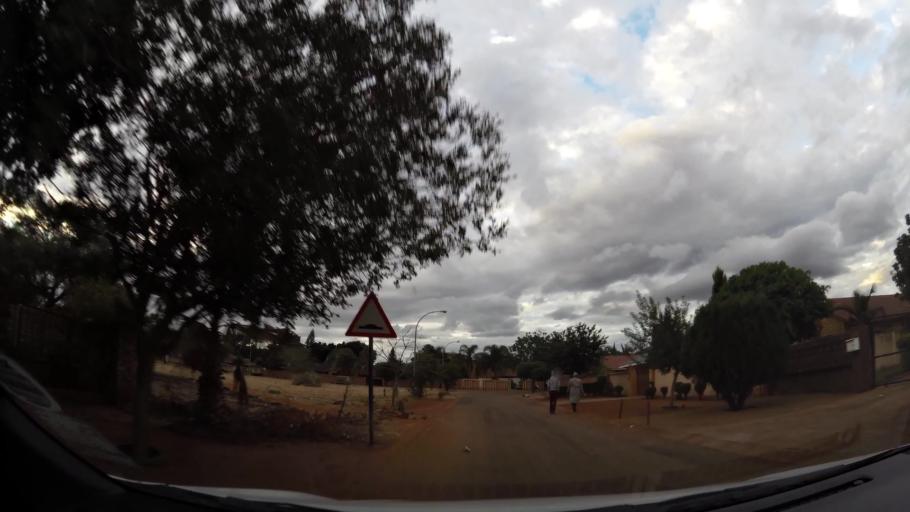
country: ZA
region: Limpopo
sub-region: Waterberg District Municipality
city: Mokopane
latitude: -24.1976
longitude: 28.9934
